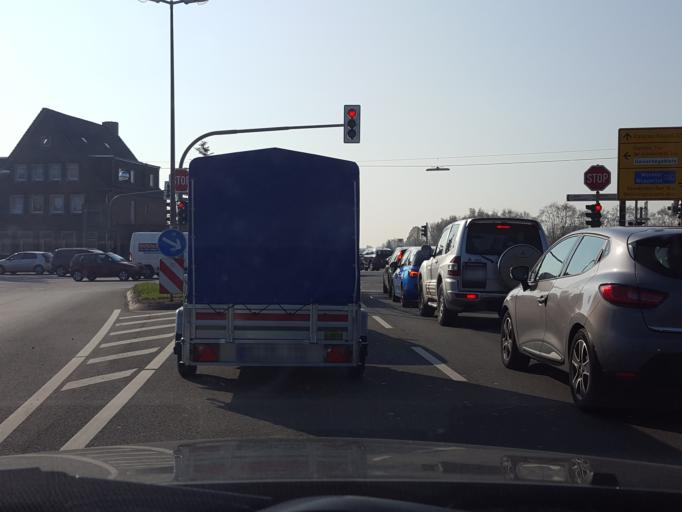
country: DE
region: North Rhine-Westphalia
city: Oer-Erkenschwick
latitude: 51.6287
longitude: 7.2461
